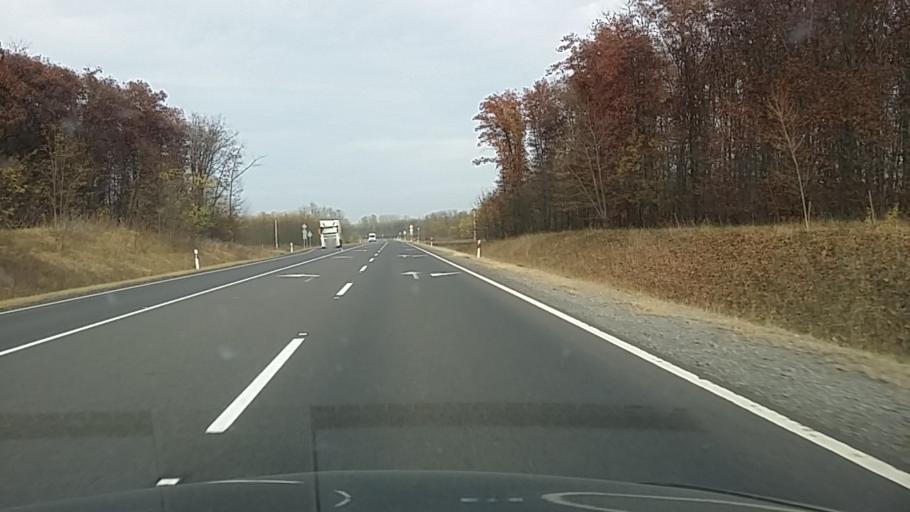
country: HU
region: Szabolcs-Szatmar-Bereg
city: Nyirpazony
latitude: 48.0009
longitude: 21.8362
